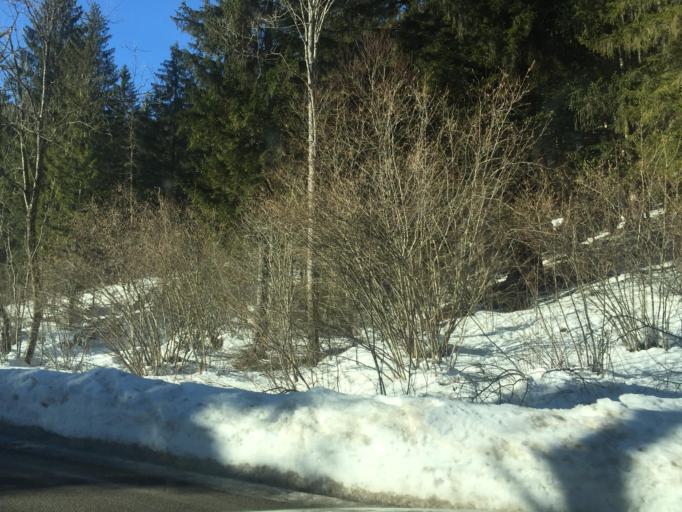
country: IT
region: Friuli Venezia Giulia
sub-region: Provincia di Udine
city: Malborghetto
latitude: 46.5026
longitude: 13.4846
